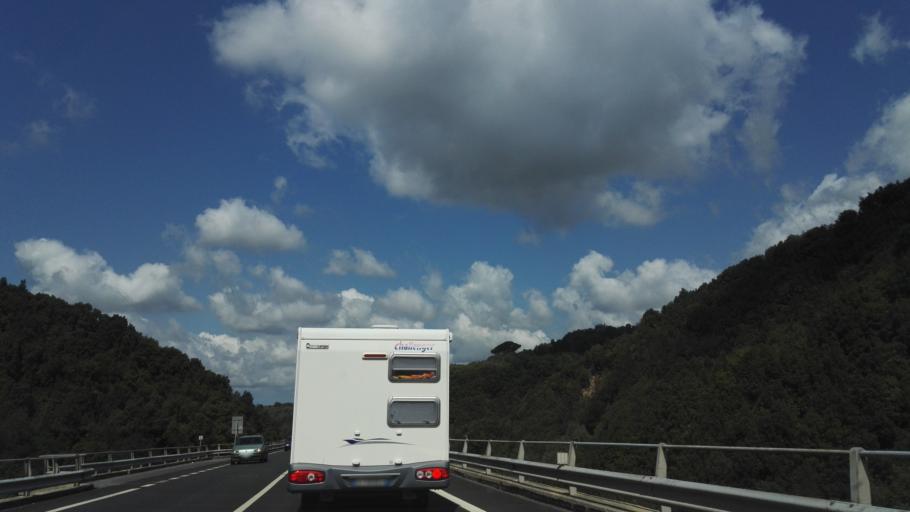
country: IT
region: Calabria
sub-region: Provincia di Reggio Calabria
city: Giffone
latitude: 38.4150
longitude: 16.1294
